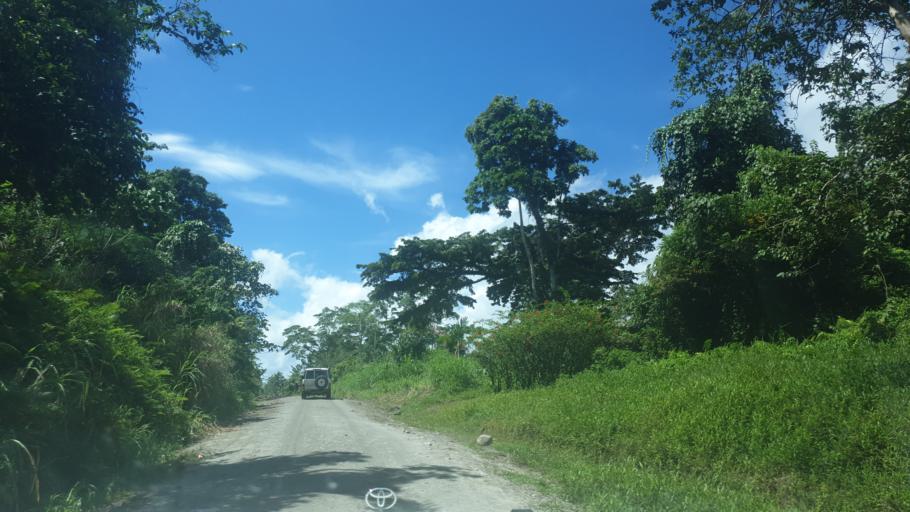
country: PG
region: Bougainville
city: Panguna
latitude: -6.6610
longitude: 155.4506
